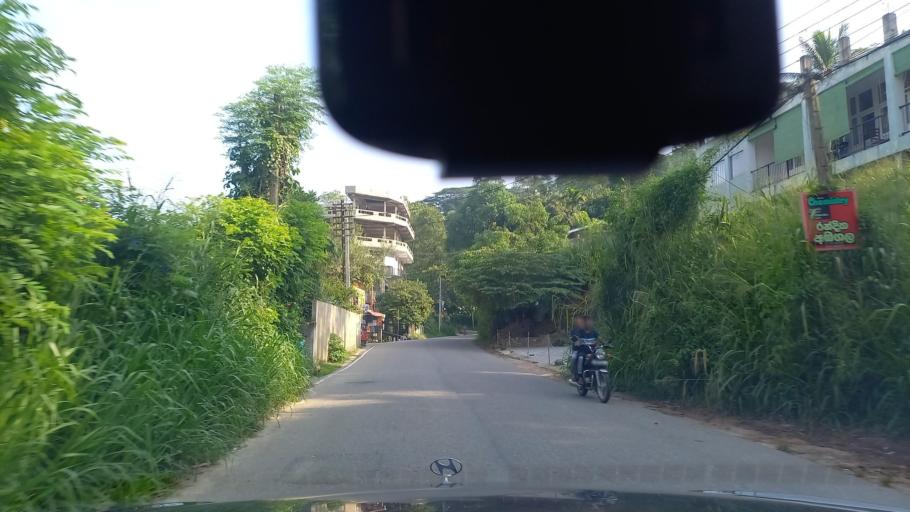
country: LK
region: Central
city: Kandy
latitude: 7.2440
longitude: 80.5987
